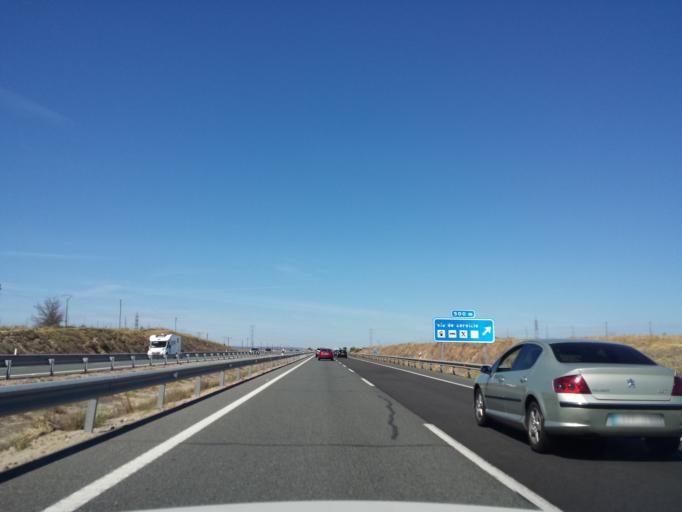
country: ES
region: Castille-La Mancha
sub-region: Province of Toledo
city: Caleruela
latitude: 39.8951
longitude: -5.3203
